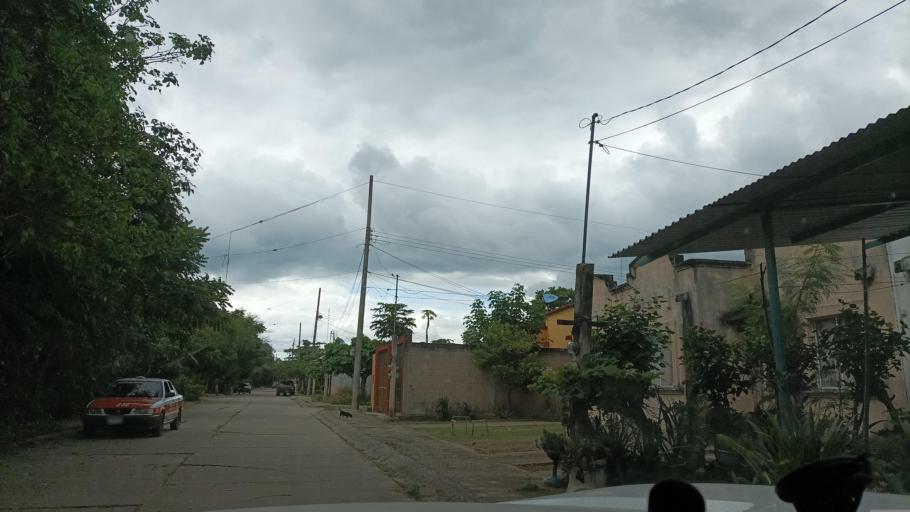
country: MX
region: Veracruz
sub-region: Soconusco
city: Fraccionamiento Santa Cruz
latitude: 17.9701
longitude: -94.8930
